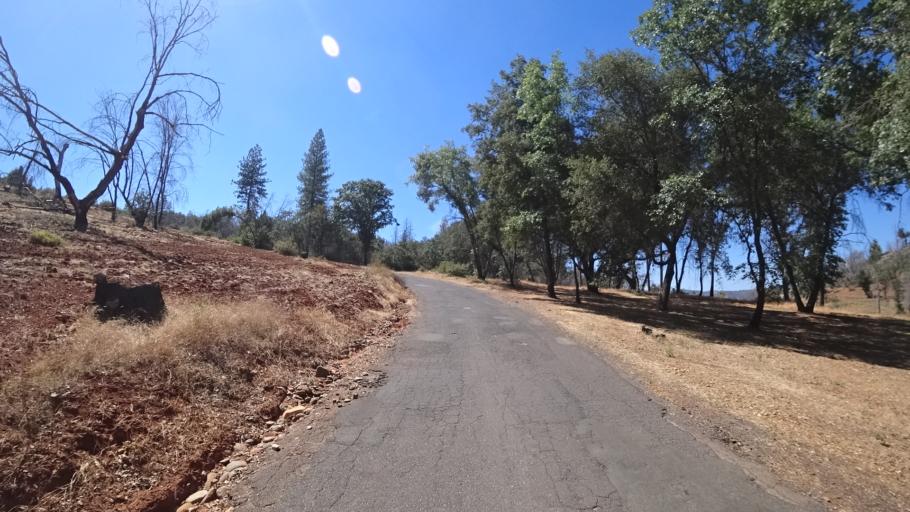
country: US
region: California
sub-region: Calaveras County
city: Mountain Ranch
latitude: 38.2881
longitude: -120.5857
